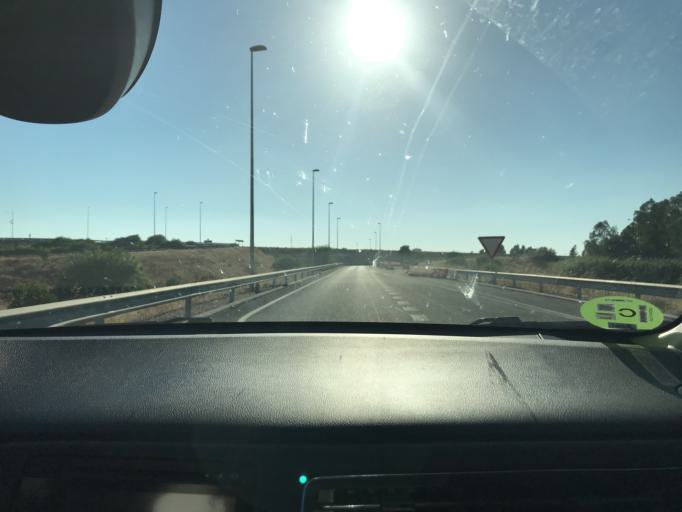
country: ES
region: Andalusia
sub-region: Provincia de Sevilla
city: Alcala de Guadaira
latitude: 37.4333
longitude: -5.8412
